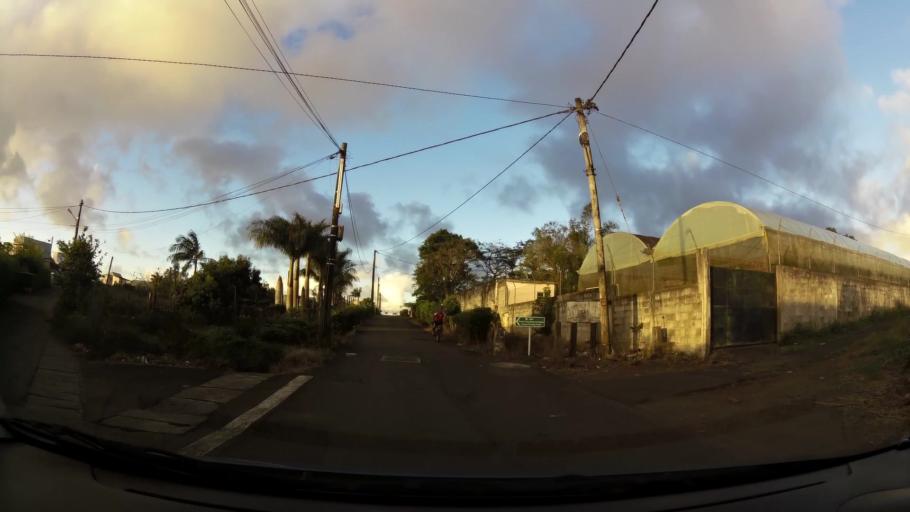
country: MU
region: Plaines Wilhems
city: Curepipe
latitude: -20.3079
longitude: 57.5321
